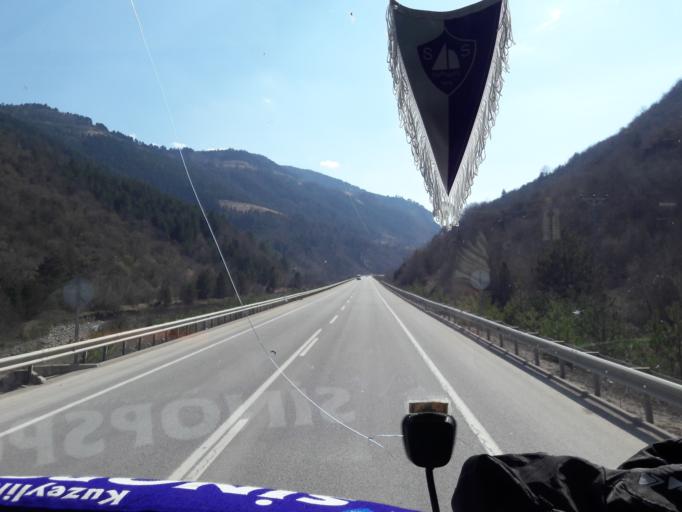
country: TR
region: Sinop
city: Erfelek
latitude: 41.7198
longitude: 34.9369
